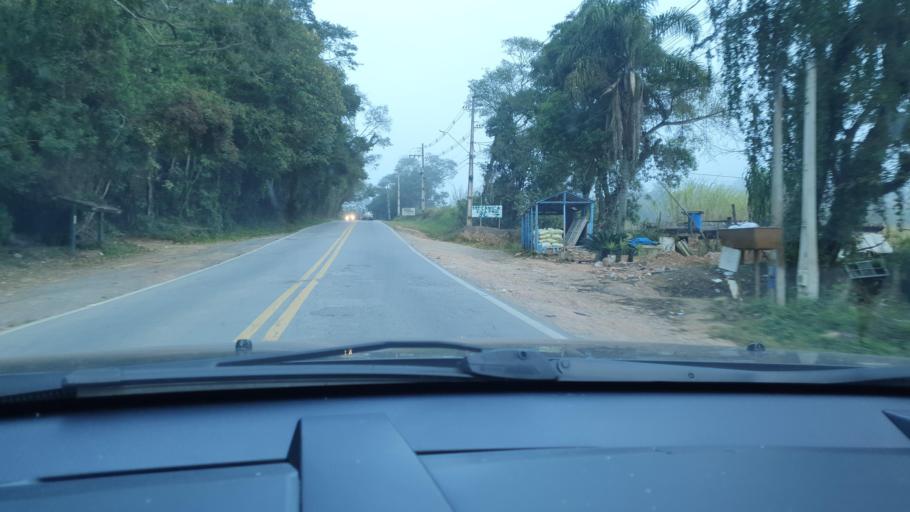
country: BR
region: Sao Paulo
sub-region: Ibiuna
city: Ibiuna
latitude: -23.6834
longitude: -47.2584
